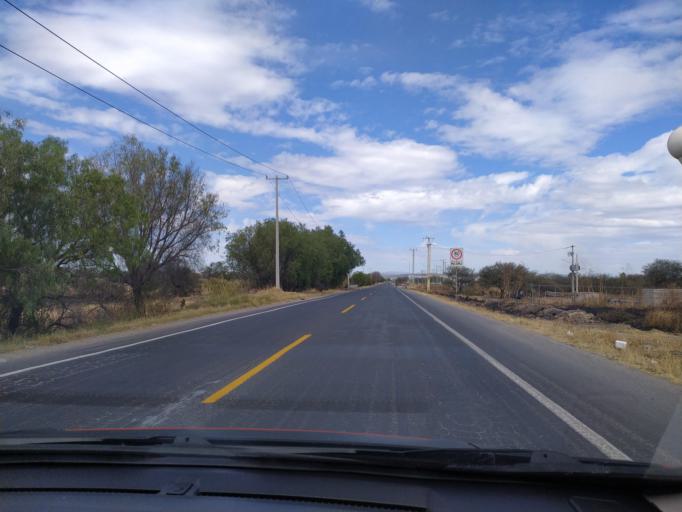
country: LA
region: Oudomxai
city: Muang La
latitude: 20.9968
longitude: 101.8335
